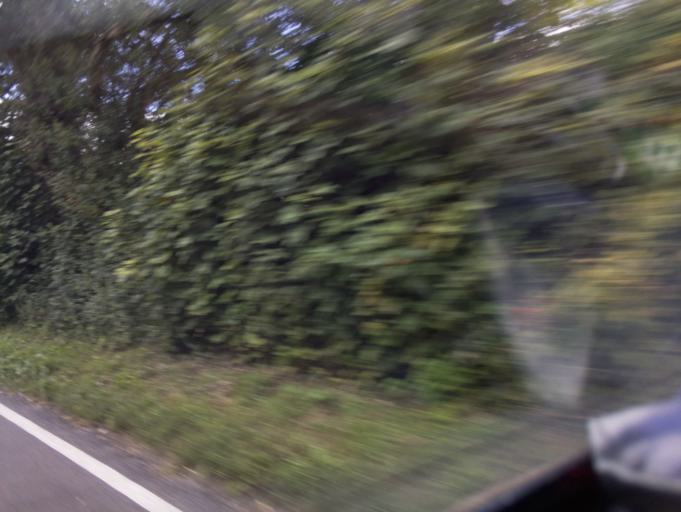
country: GB
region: England
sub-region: Hampshire
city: Winchester
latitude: 51.0998
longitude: -1.3980
